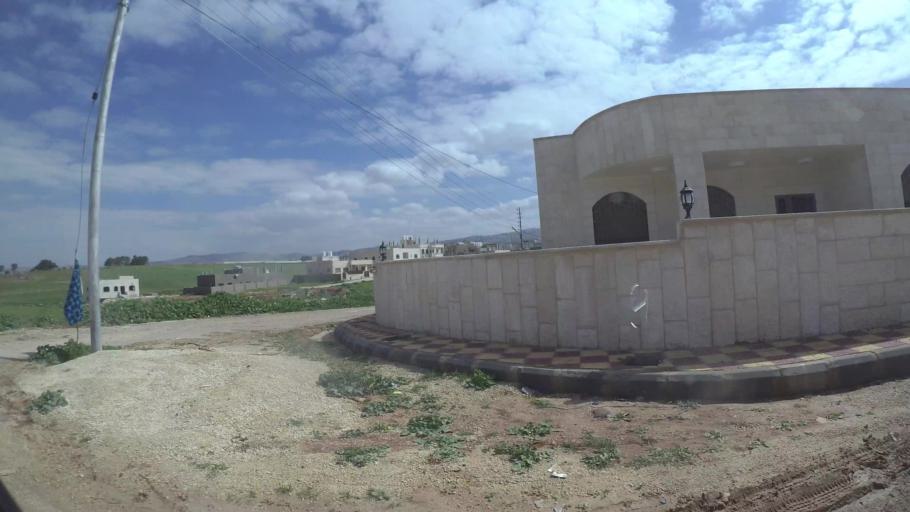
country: JO
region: Amman
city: Al Jubayhah
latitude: 32.0667
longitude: 35.8209
